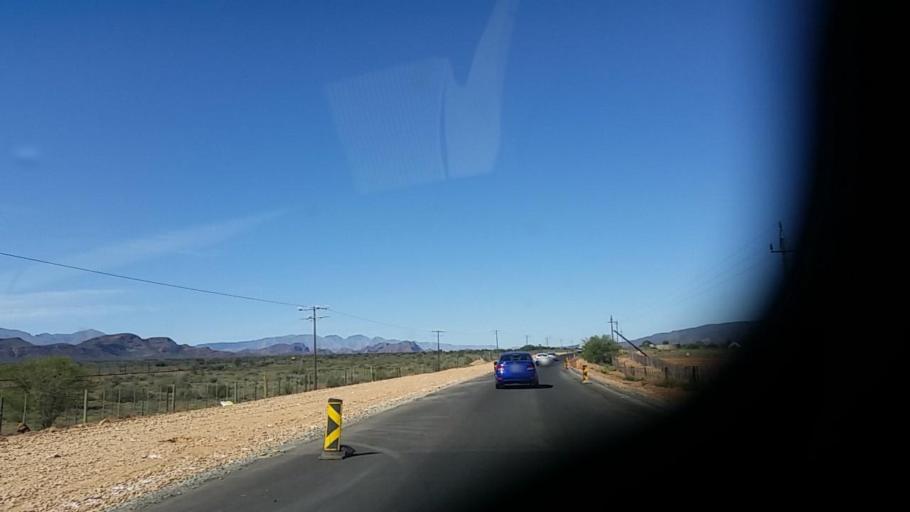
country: ZA
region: Western Cape
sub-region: Eden District Municipality
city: Oudtshoorn
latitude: -33.5769
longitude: 22.3267
